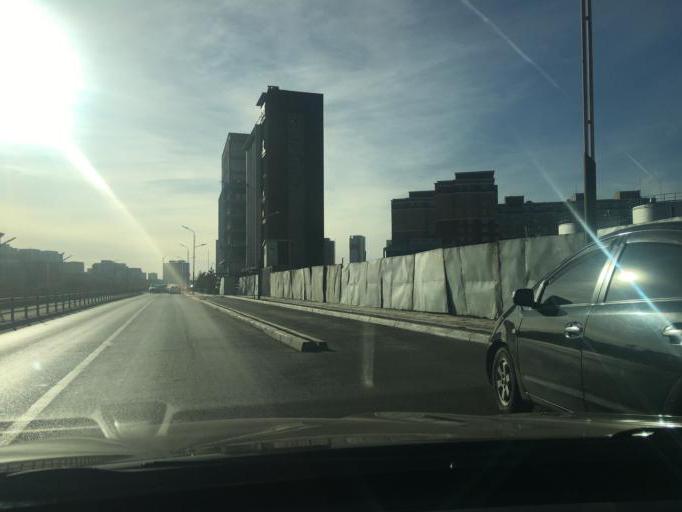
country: MN
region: Ulaanbaatar
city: Ulaanbaatar
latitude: 47.9060
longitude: 106.9081
